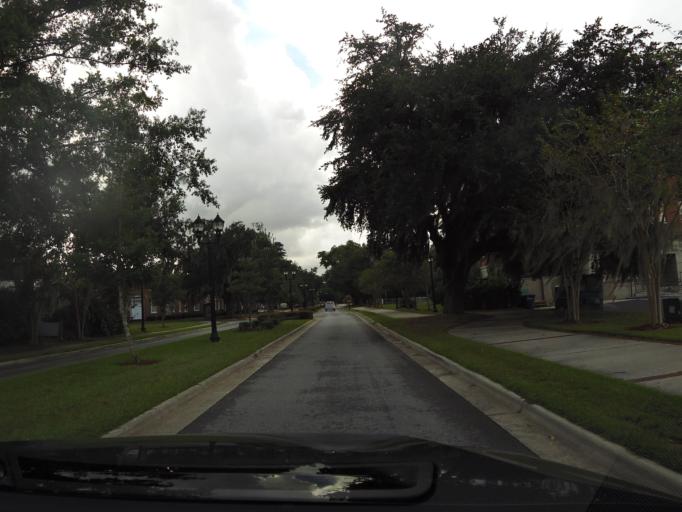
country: US
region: Georgia
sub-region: Liberty County
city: Hinesville
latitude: 31.8492
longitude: -81.5914
